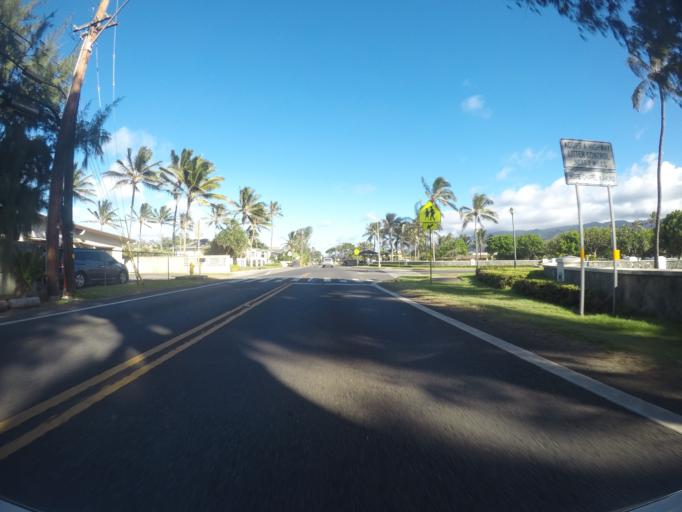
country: US
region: Hawaii
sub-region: Honolulu County
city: La'ie
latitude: 21.6493
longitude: -157.9237
